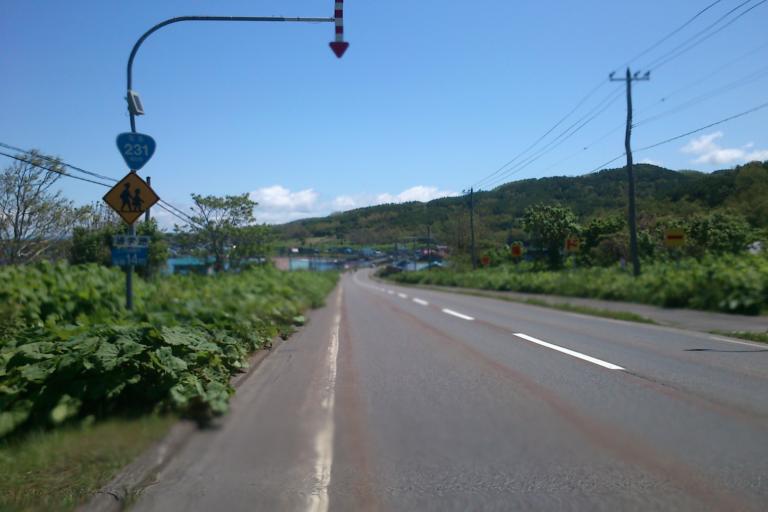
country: JP
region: Hokkaido
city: Rumoi
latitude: 43.8346
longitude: 141.4847
